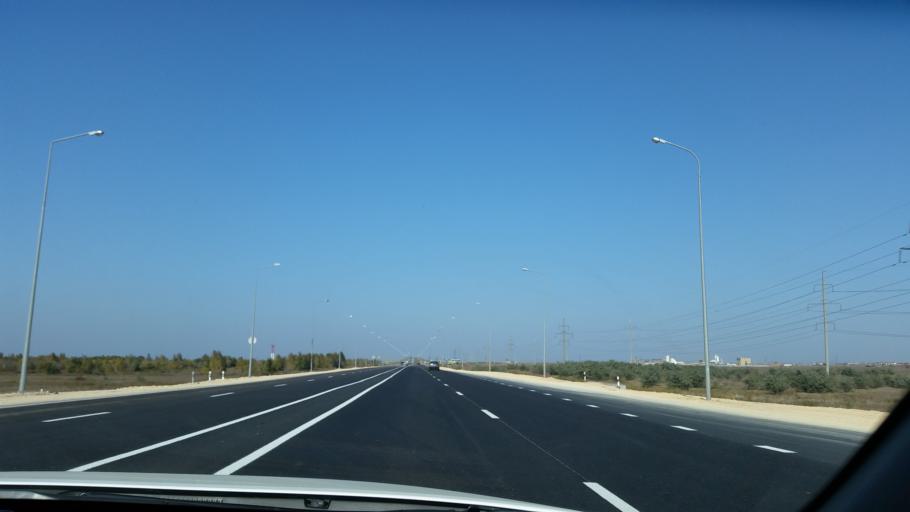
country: KZ
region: Astana Qalasy
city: Astana
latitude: 51.2114
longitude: 71.3157
